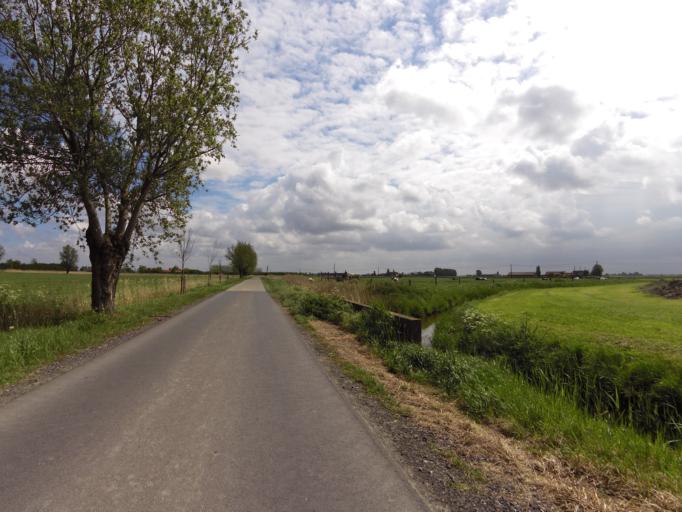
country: BE
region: Flanders
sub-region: Provincie West-Vlaanderen
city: Middelkerke
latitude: 51.1326
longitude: 2.8502
